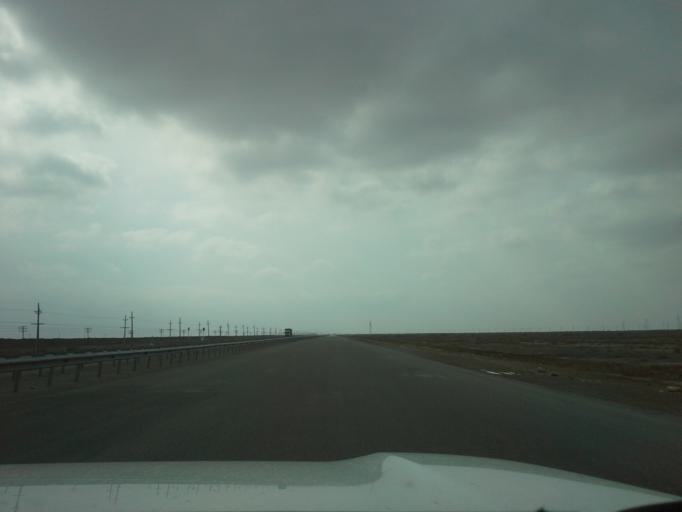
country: IR
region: Razavi Khorasan
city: Kalat-e Naderi
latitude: 37.2114
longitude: 60.0764
